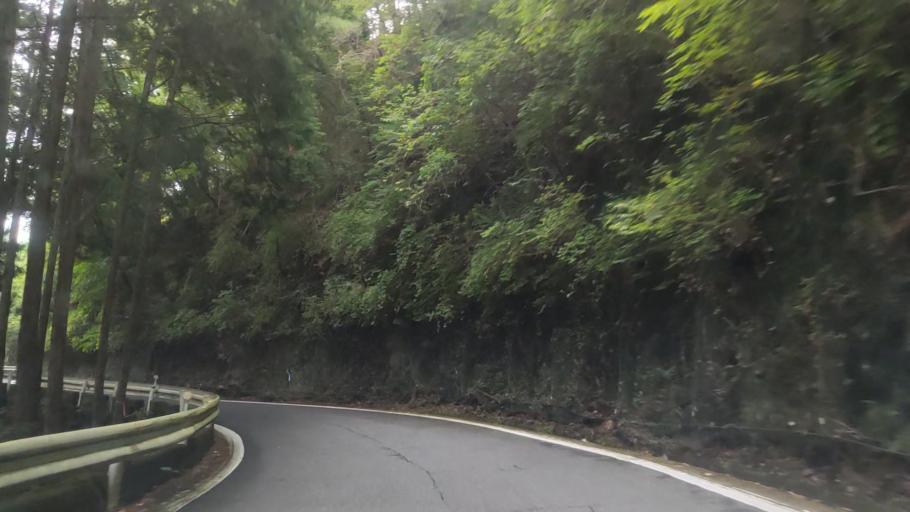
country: JP
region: Wakayama
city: Koya
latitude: 34.2378
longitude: 135.5478
